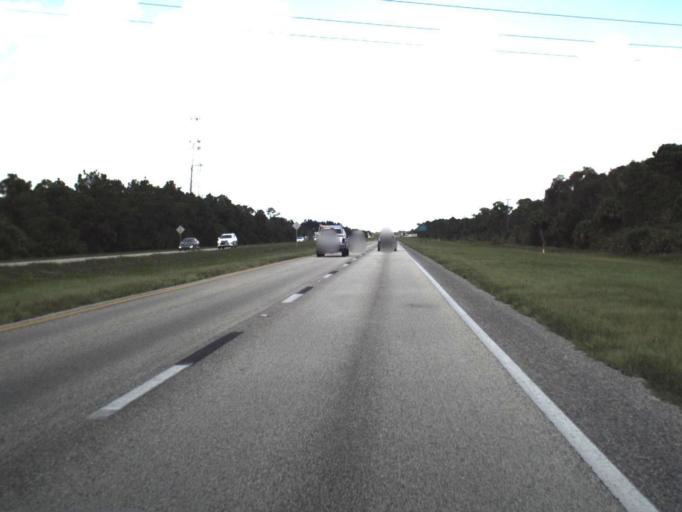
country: US
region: Florida
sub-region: Lee County
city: Burnt Store Marina
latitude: 26.8353
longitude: -81.9730
